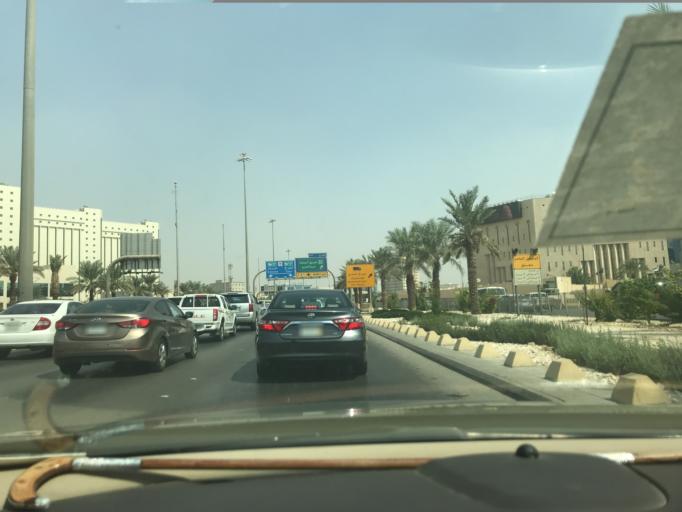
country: SA
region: Ar Riyad
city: Riyadh
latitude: 24.6861
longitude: 46.7062
